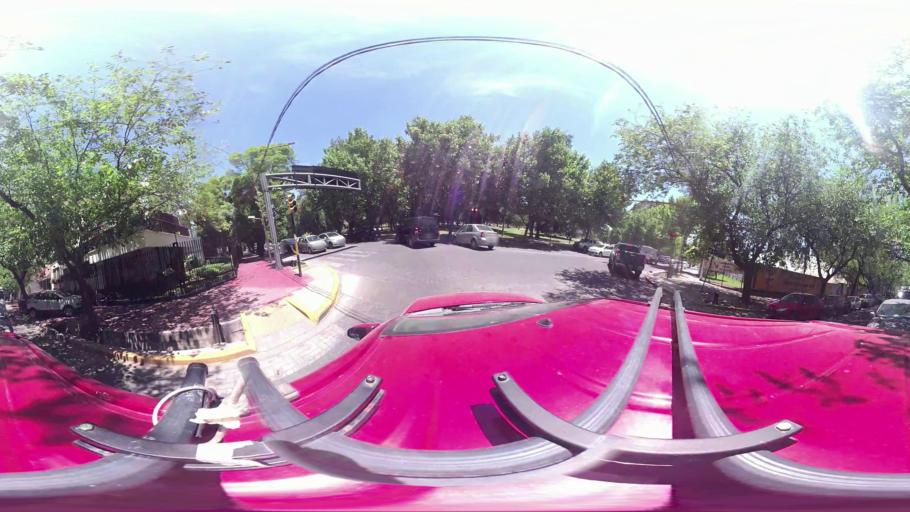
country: AR
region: Mendoza
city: Mendoza
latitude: -32.8995
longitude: -68.8540
